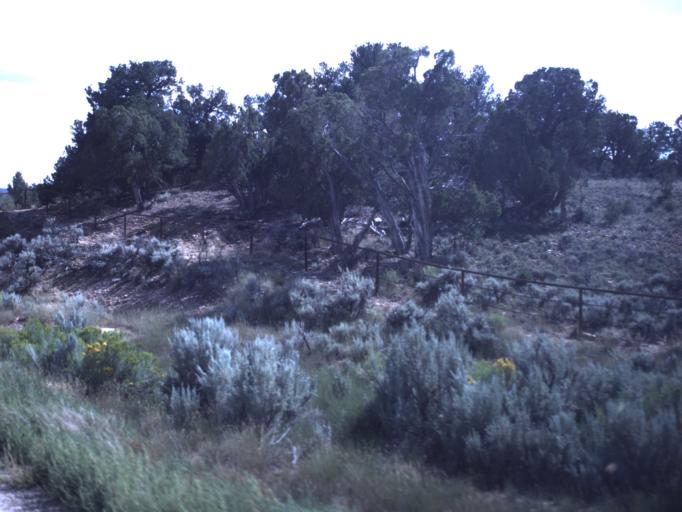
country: US
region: Utah
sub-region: Duchesne County
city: Duchesne
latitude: 40.2760
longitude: -110.7027
